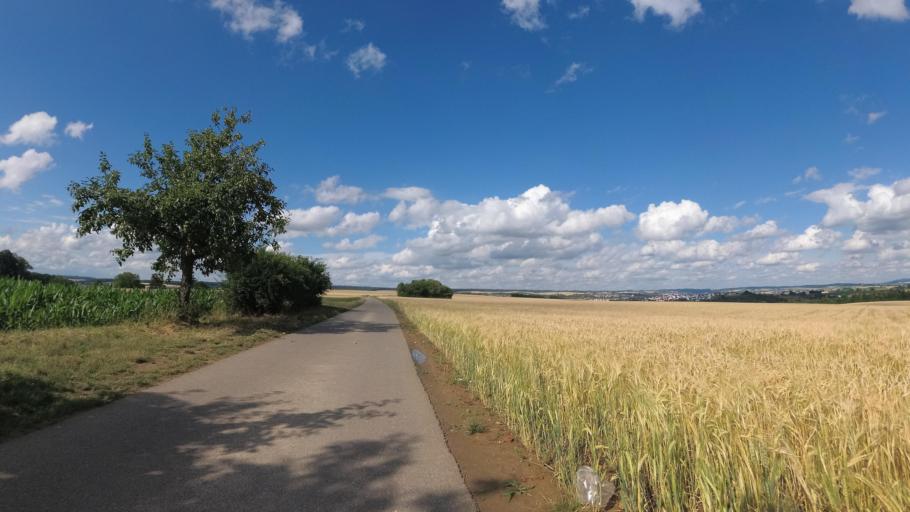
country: DE
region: Baden-Wuerttemberg
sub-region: Regierungsbezirk Stuttgart
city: Neuenstadt am Kocher
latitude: 49.2251
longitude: 9.3091
